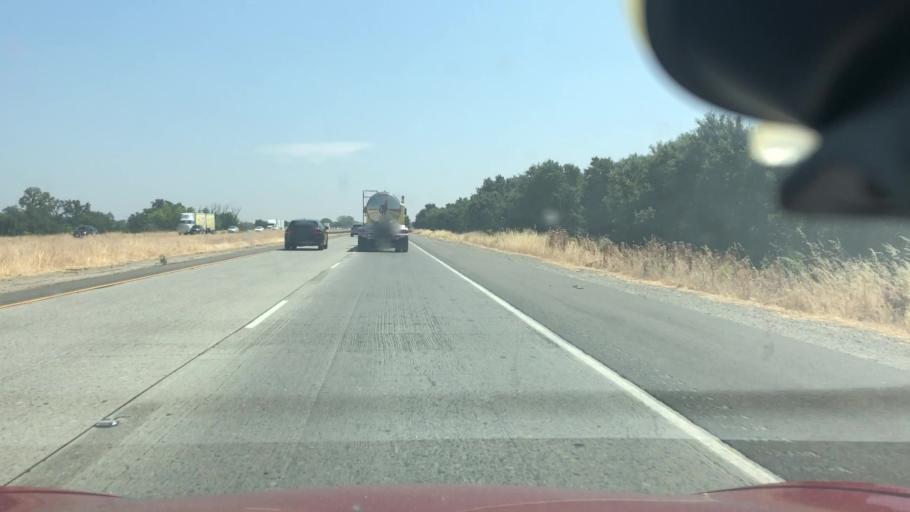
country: US
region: California
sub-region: San Joaquin County
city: Thornton
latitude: 38.2670
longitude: -121.4528
